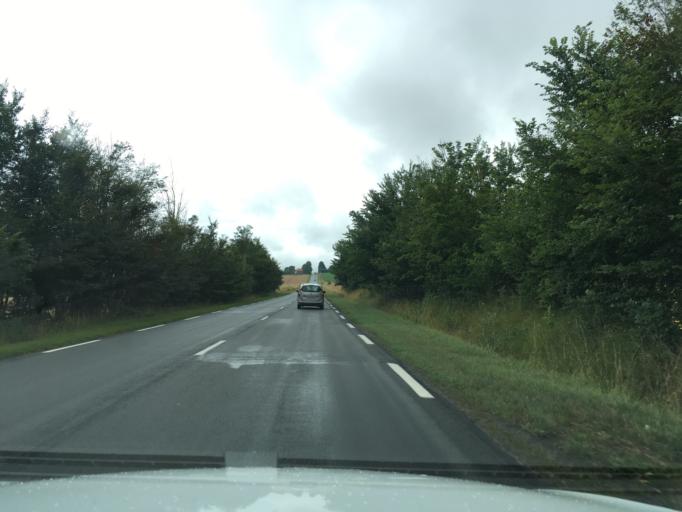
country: FR
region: Picardie
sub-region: Departement de l'Aisne
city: Homblieres
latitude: 49.8438
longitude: 3.4102
